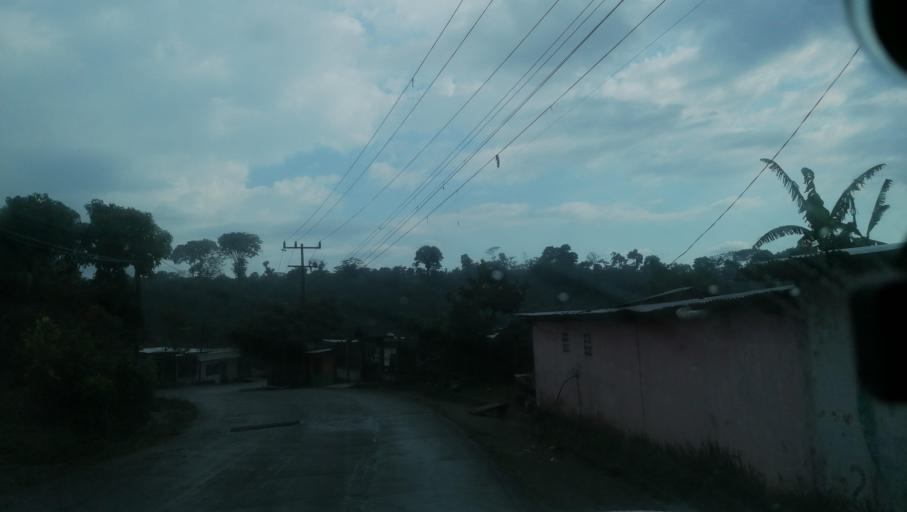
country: MX
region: Chiapas
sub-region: Cacahoatan
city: Benito Juarez
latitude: 15.0514
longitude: -92.1893
